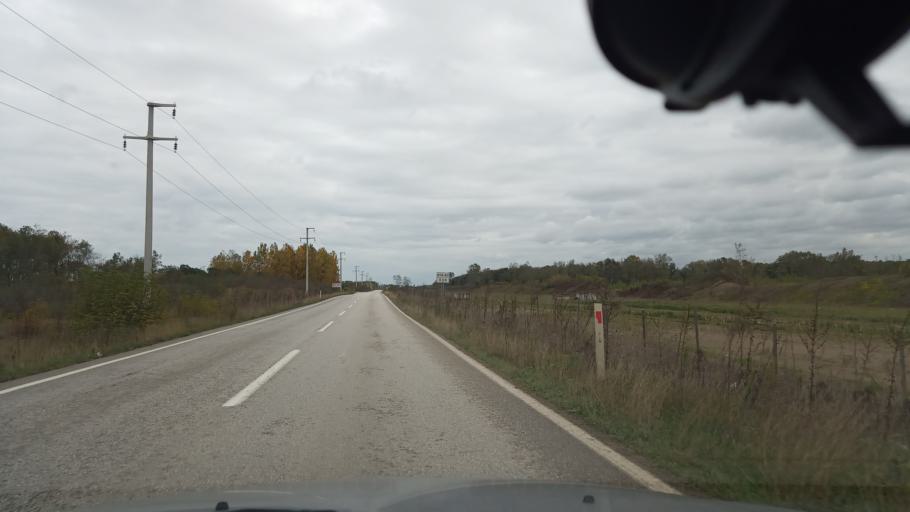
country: TR
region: Sakarya
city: Karasu
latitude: 41.1214
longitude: 30.5805
